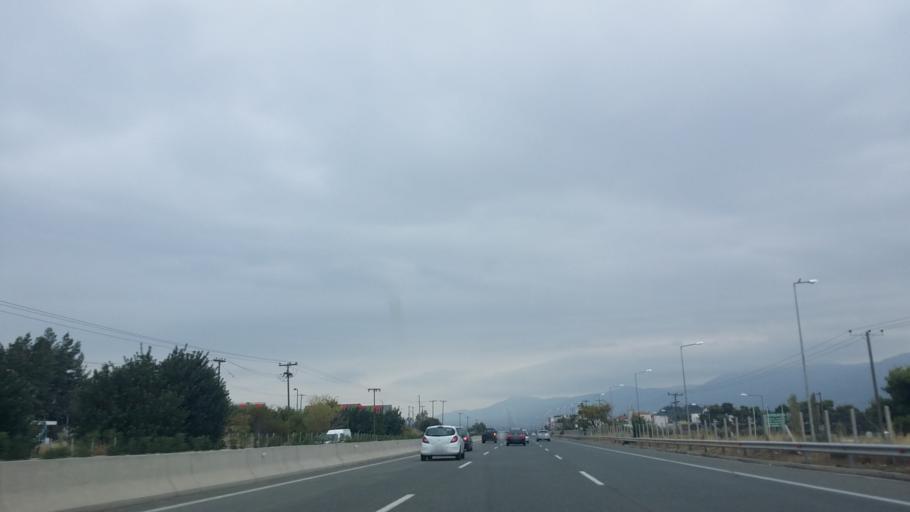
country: GR
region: Central Greece
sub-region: Nomos Voiotias
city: Oinofyta
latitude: 38.3159
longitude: 23.6298
